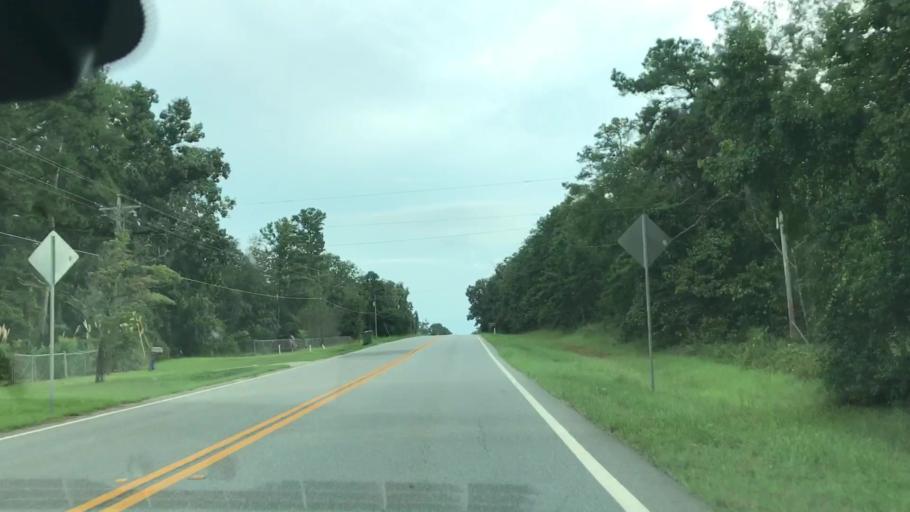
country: US
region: Georgia
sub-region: Quitman County
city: Georgetown
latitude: 31.8587
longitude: -85.0691
